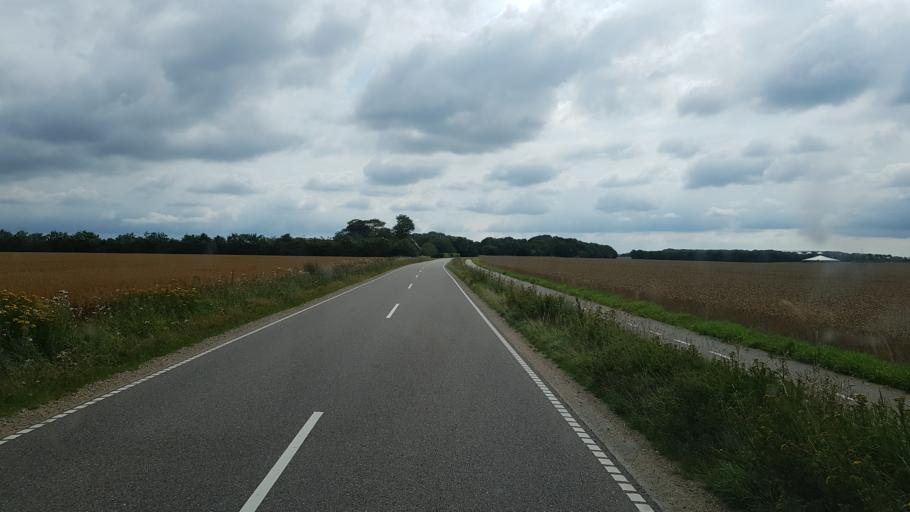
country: DK
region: South Denmark
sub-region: Varde Kommune
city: Varde
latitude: 55.7499
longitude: 8.4678
